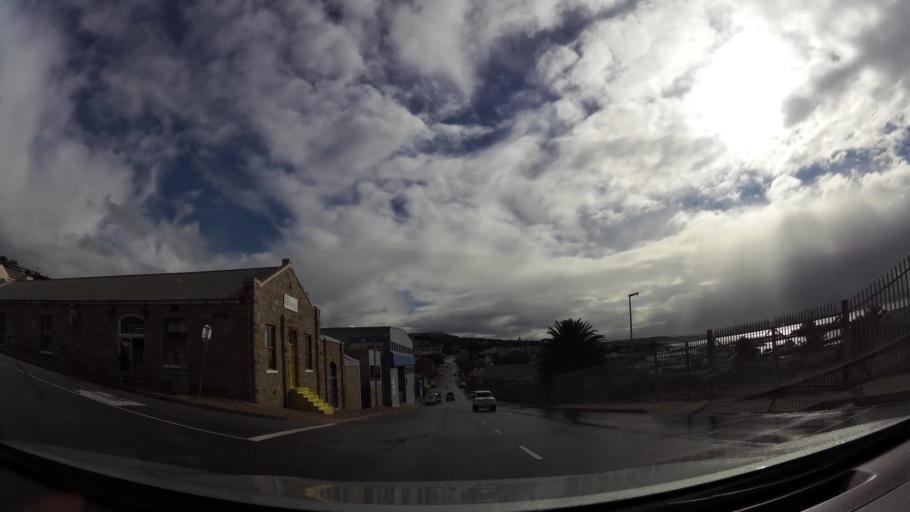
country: ZA
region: Western Cape
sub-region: Eden District Municipality
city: Mossel Bay
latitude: -34.1817
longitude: 22.1496
